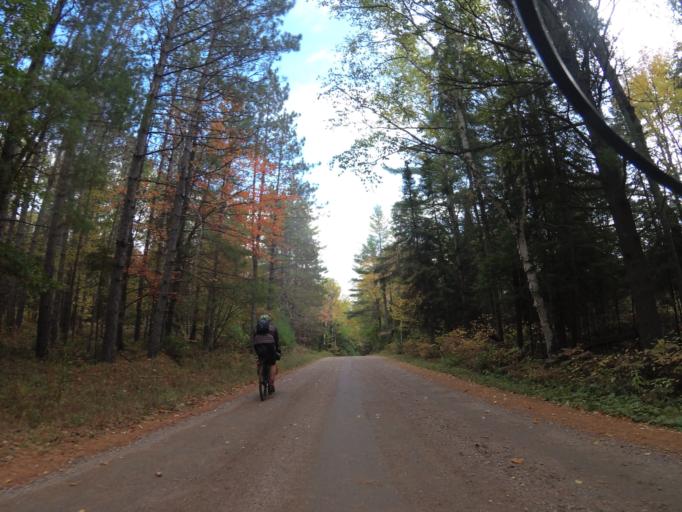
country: CA
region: Ontario
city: Pembroke
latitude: 45.2630
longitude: -77.2130
